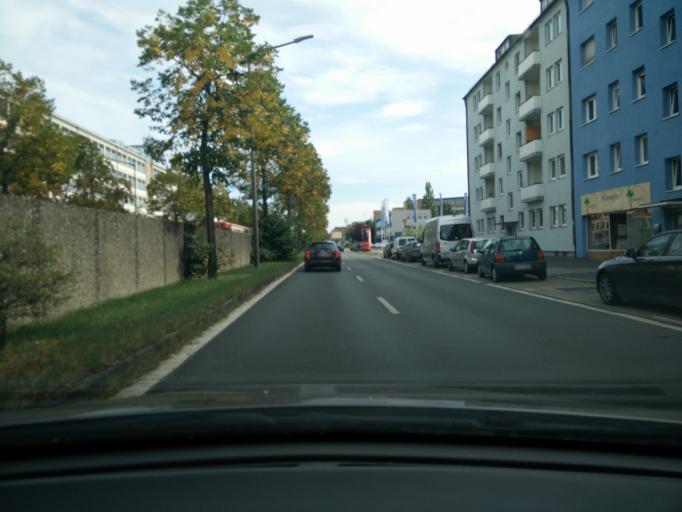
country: DE
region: Bavaria
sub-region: Regierungsbezirk Mittelfranken
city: Wetzendorf
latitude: 49.4598
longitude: 11.0280
